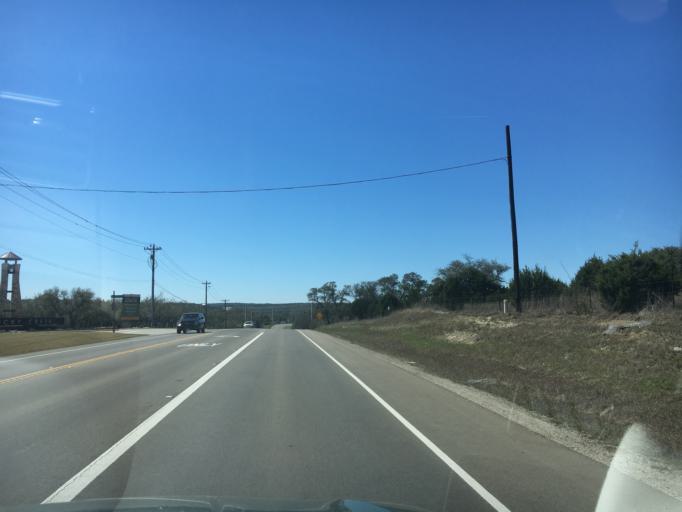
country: US
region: Texas
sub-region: Travis County
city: The Hills
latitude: 30.2919
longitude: -98.0337
